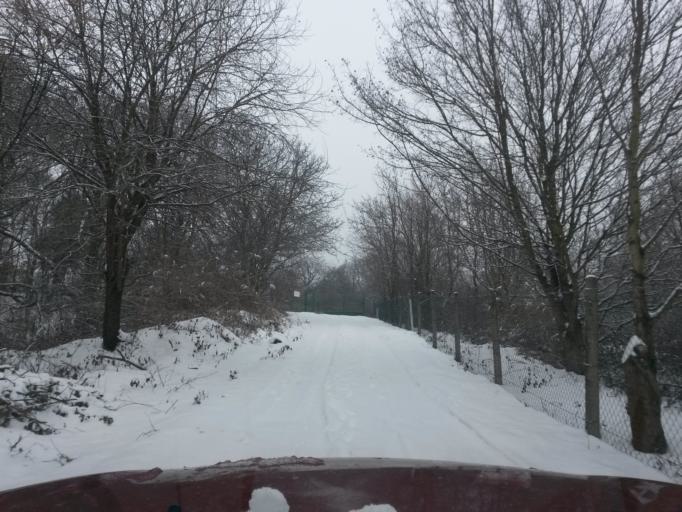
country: SK
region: Kosicky
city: Kosice
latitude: 48.7252
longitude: 21.3266
